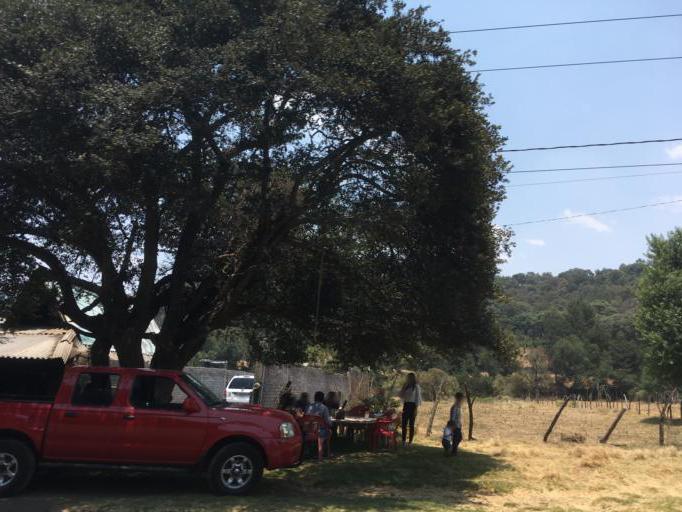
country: MX
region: Michoacan
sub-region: Morelia
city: Iratzio
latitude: 19.6236
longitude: -101.4627
